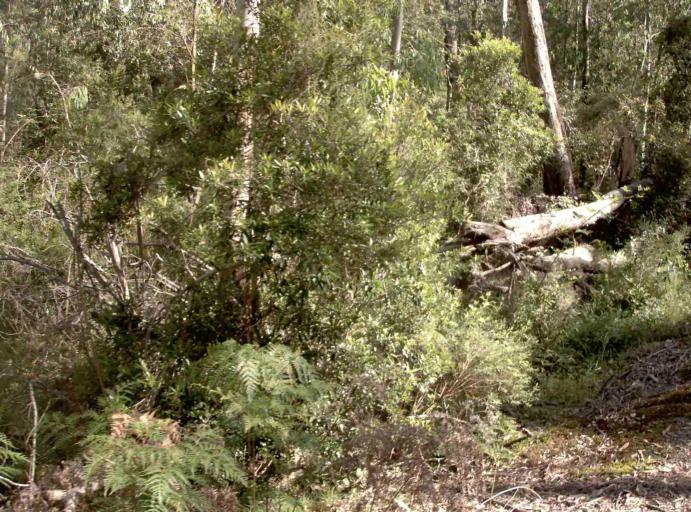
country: AU
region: Victoria
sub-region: East Gippsland
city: Lakes Entrance
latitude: -37.4658
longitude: 148.5631
